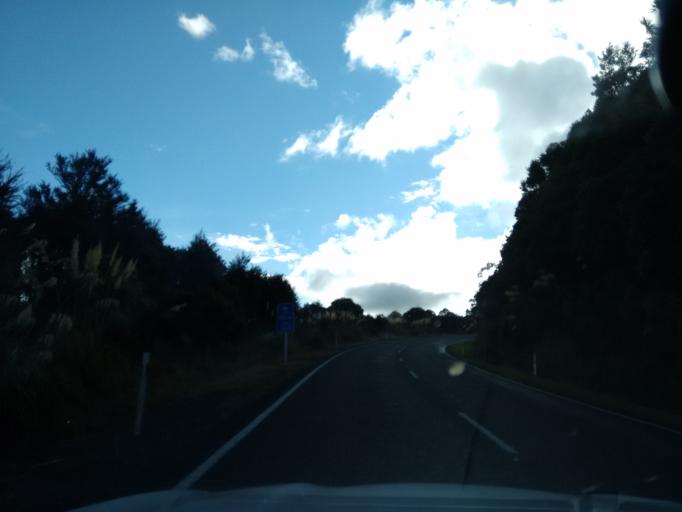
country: NZ
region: Waikato
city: Turangi
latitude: -39.0224
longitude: 175.7186
